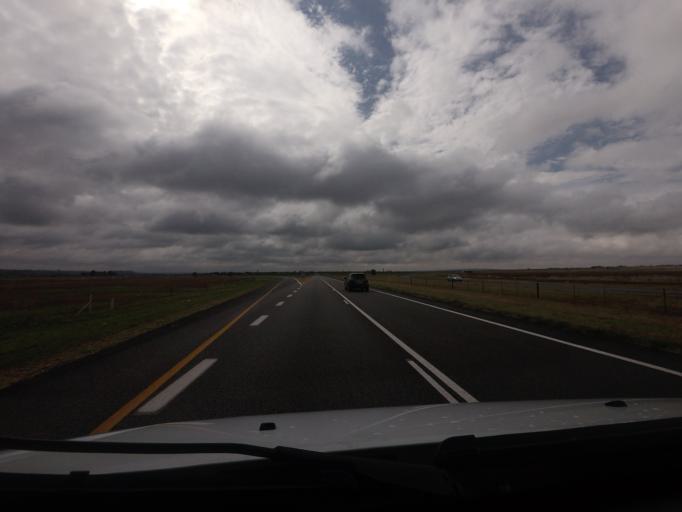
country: ZA
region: Gauteng
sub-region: City of Tshwane Metropolitan Municipality
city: Bronkhorstspruit
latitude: -25.8060
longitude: 28.6903
